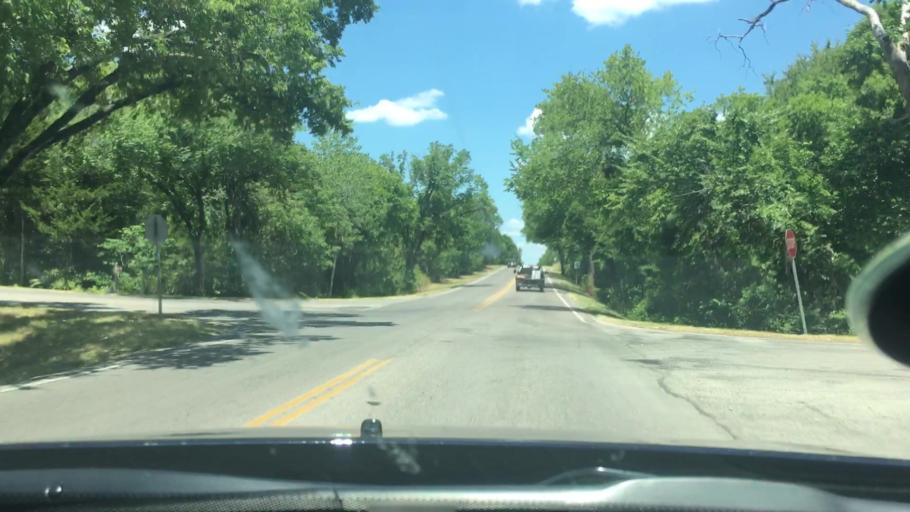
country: US
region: Oklahoma
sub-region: Murray County
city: Sulphur
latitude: 34.4936
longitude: -96.9677
